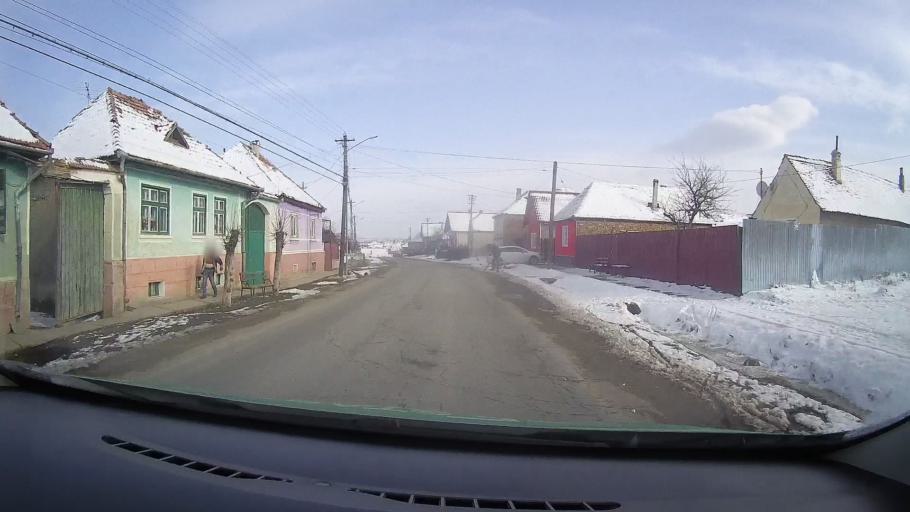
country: RO
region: Sibiu
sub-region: Comuna Merghindeal
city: Merghindeal
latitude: 45.9666
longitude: 24.7162
